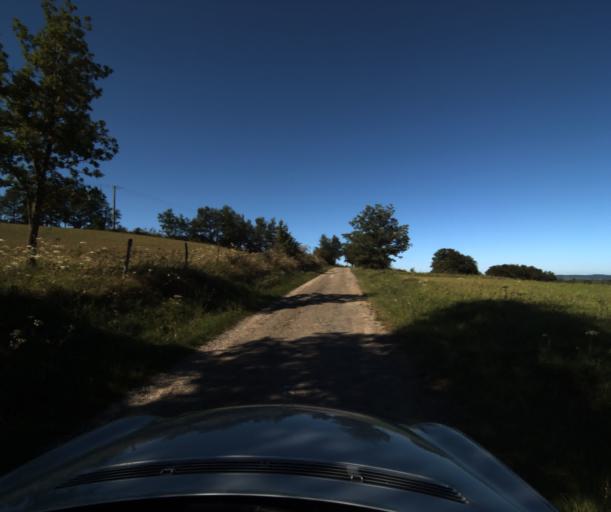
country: FR
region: Midi-Pyrenees
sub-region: Departement de l'Ariege
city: Lavelanet
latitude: 42.9721
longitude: 1.8886
